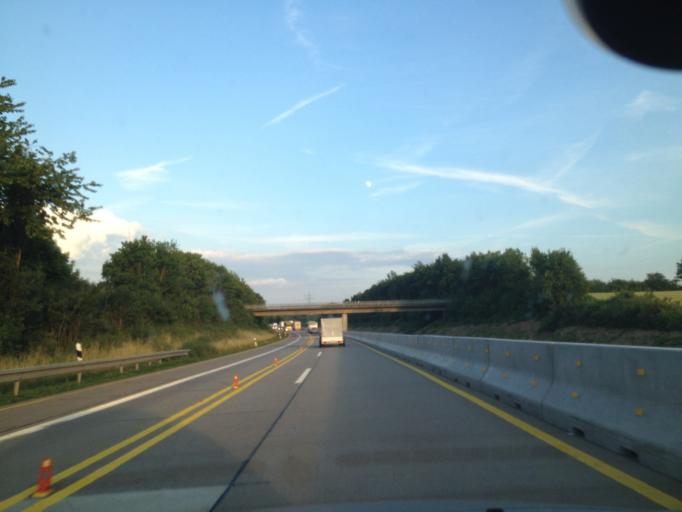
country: DE
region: Bavaria
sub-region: Regierungsbezirk Mittelfranken
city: Gollhofen
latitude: 49.5397
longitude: 10.1706
